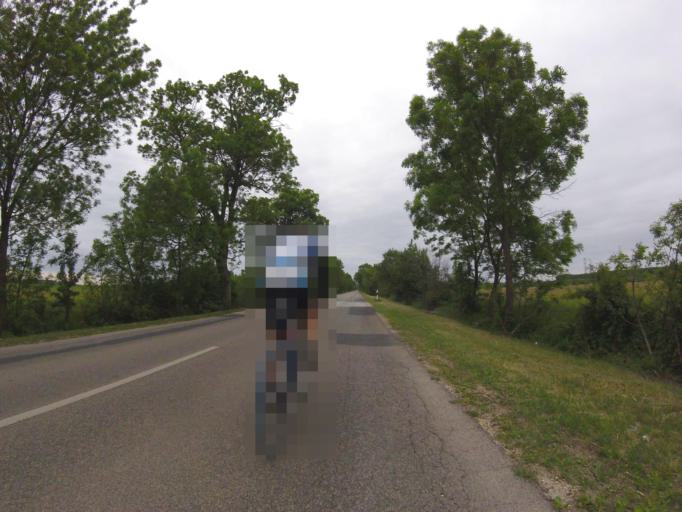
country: HU
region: Pest
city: Ujhartyan
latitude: 47.2292
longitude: 19.3784
